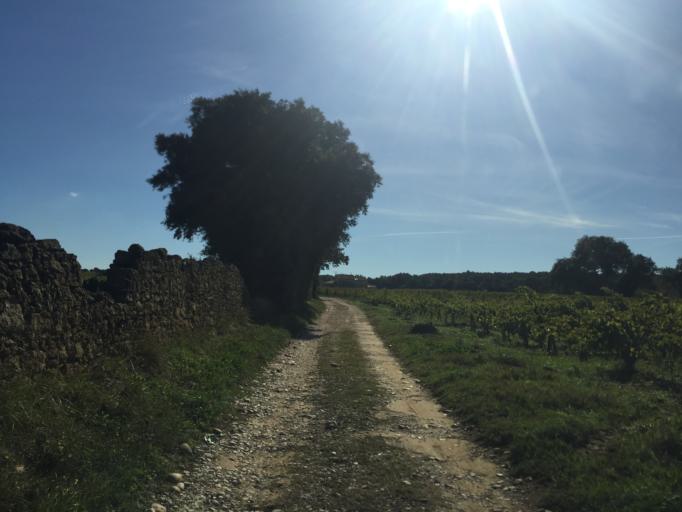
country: FR
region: Provence-Alpes-Cote d'Azur
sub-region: Departement du Vaucluse
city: Courthezon
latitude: 44.0856
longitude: 4.8520
